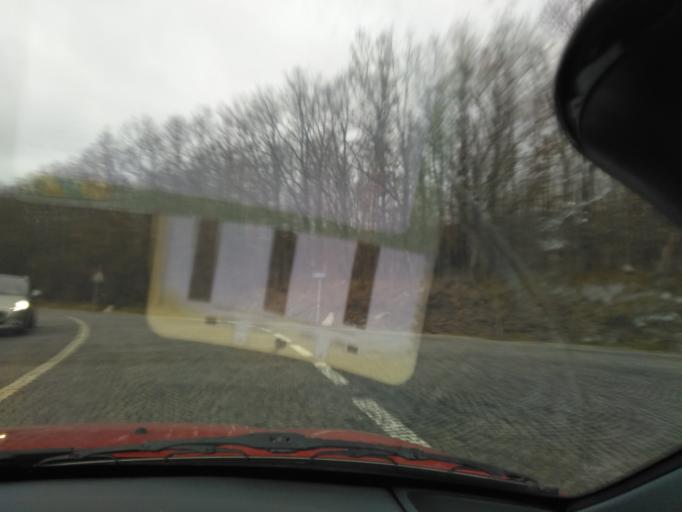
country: AT
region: Lower Austria
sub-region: Politischer Bezirk Wien-Umgebung
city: Klosterneuburg
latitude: 48.2507
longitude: 16.2862
